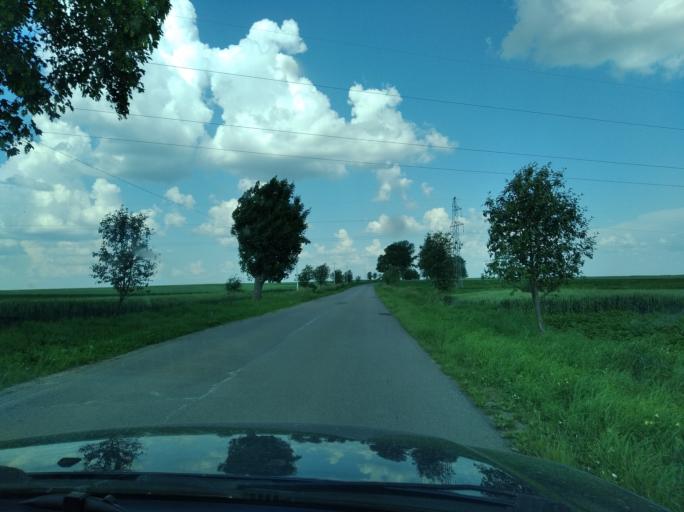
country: PL
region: Subcarpathian Voivodeship
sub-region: Powiat jaroslawski
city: Ostrow
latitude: 49.9427
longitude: 22.7548
